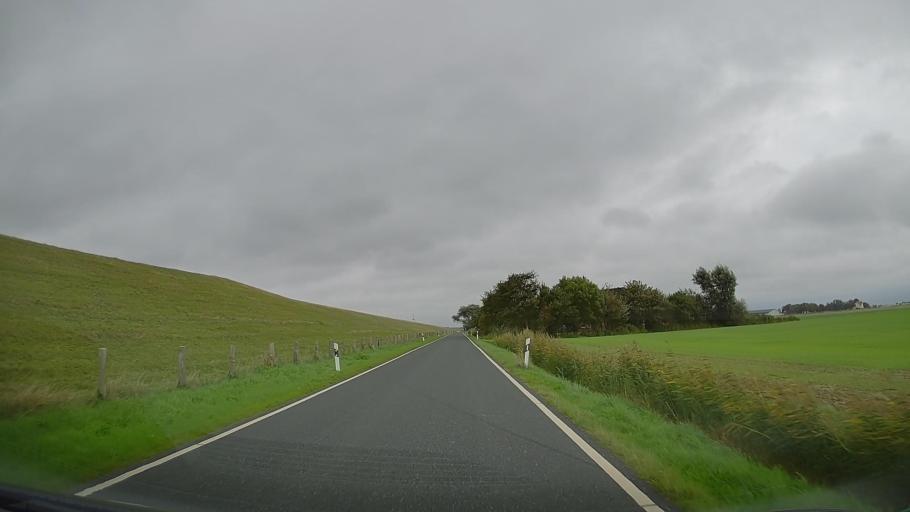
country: DE
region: Schleswig-Holstein
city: Friedrichskoog
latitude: 54.0271
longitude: 8.9215
